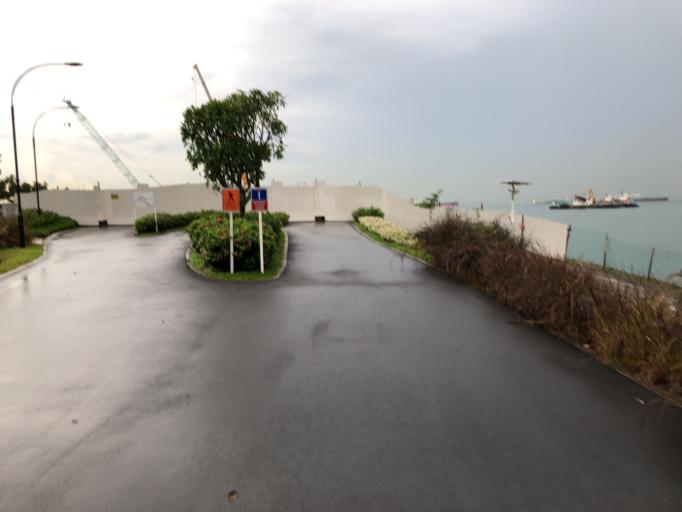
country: SG
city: Singapore
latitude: 1.2818
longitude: 103.8745
